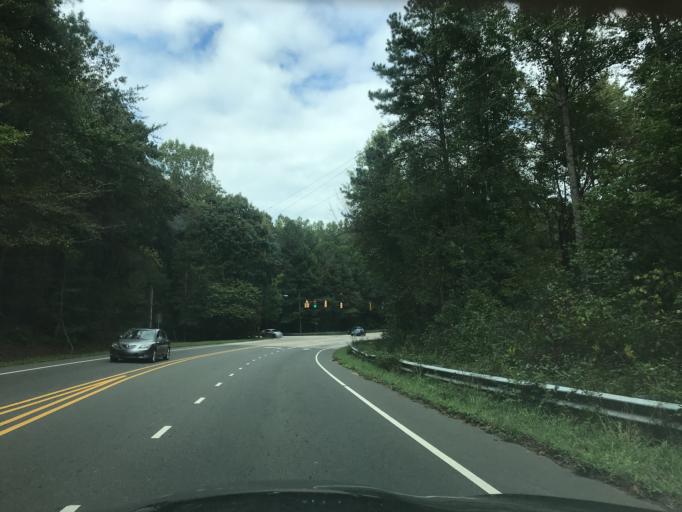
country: US
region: North Carolina
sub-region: Orange County
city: Chapel Hill
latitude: 35.9281
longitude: -79.0676
